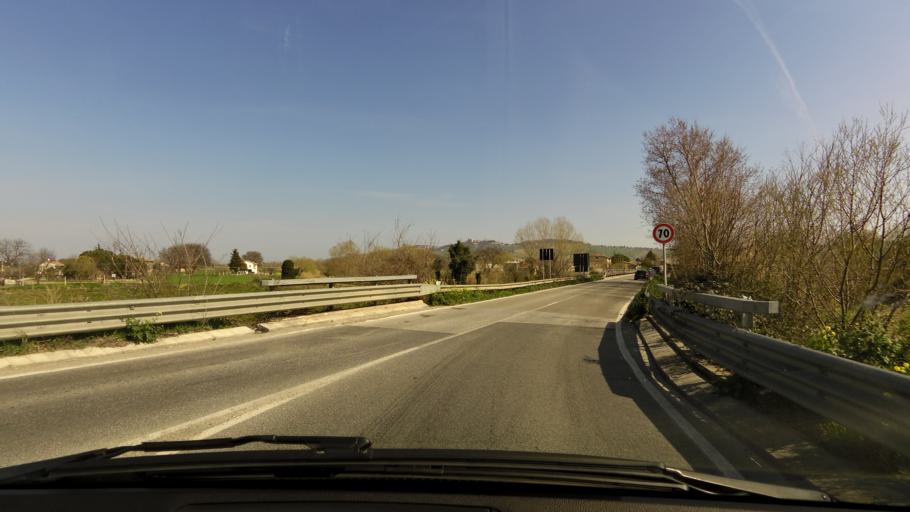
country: IT
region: The Marches
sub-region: Provincia di Macerata
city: Montelupone
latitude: 43.3747
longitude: 13.5767
